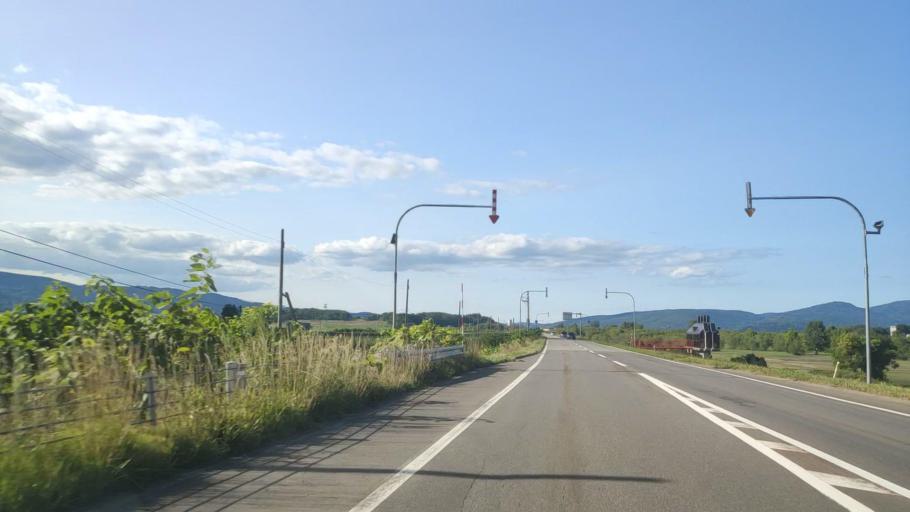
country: JP
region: Hokkaido
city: Nayoro
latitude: 44.8040
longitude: 142.0674
